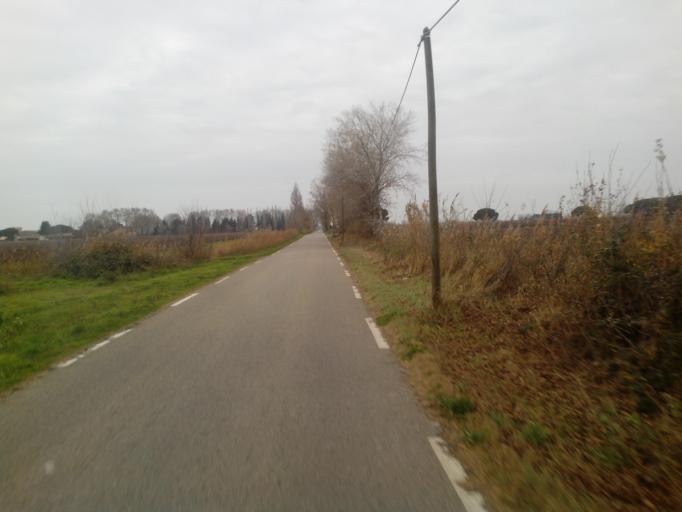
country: FR
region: Languedoc-Roussillon
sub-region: Departement du Gard
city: Vauvert
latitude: 43.5808
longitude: 4.3347
